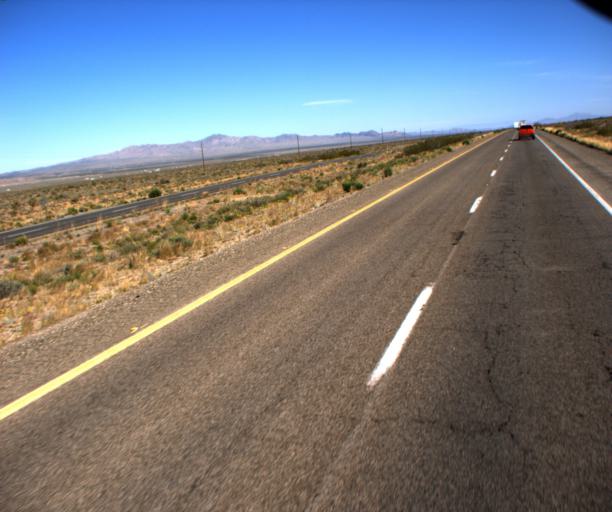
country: US
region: Arizona
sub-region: Mohave County
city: Dolan Springs
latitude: 35.4646
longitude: -114.3073
